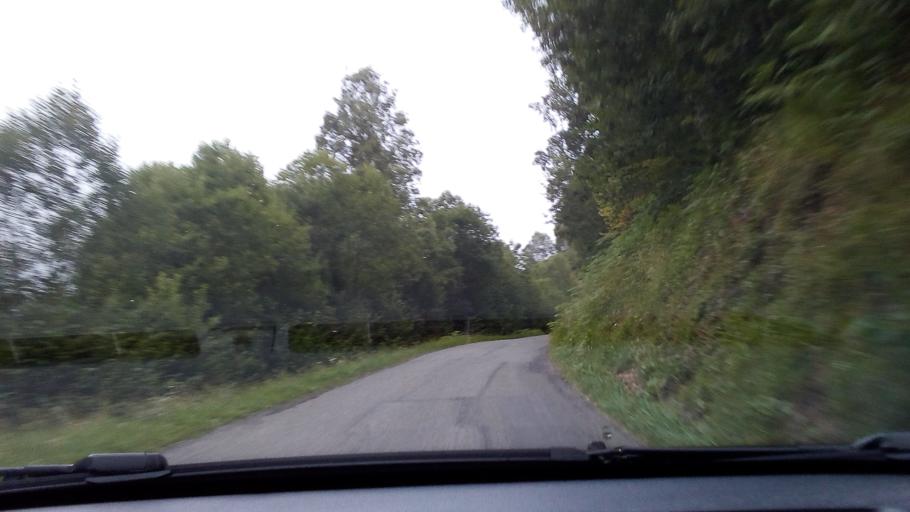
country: FR
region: Midi-Pyrenees
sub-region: Departement des Hautes-Pyrenees
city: Cauterets
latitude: 42.9466
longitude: -0.2137
